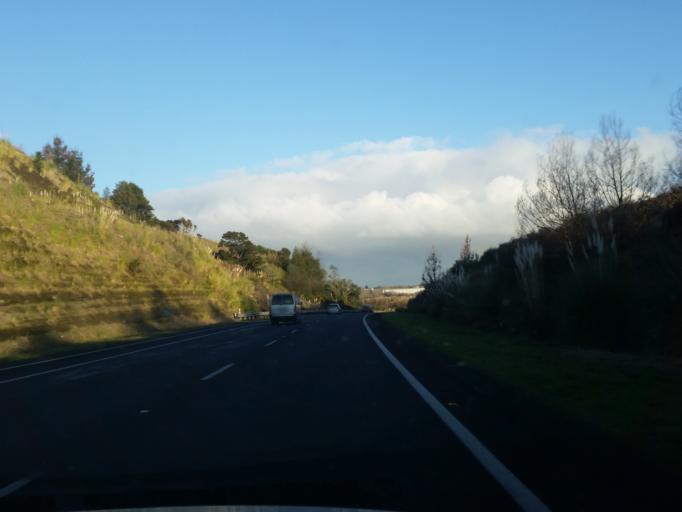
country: NZ
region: Auckland
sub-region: Auckland
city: Pukekohe East
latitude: -37.2912
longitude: 175.0587
